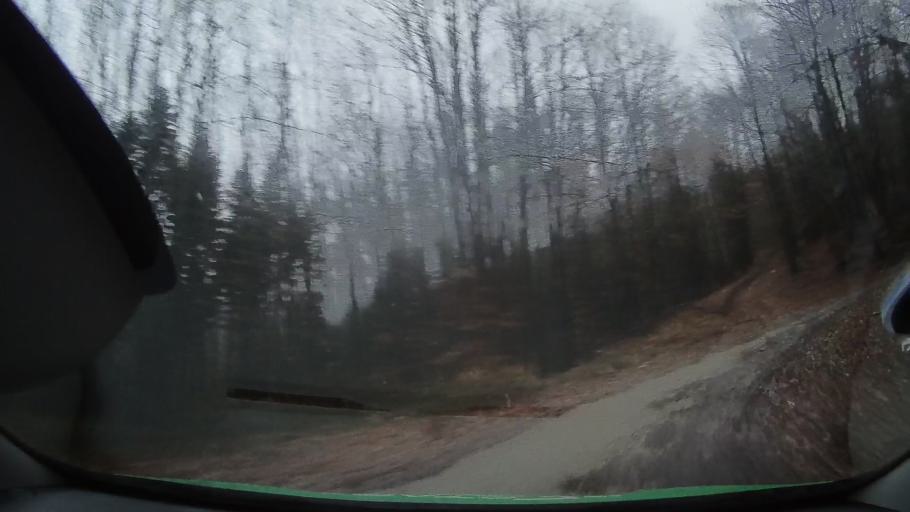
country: RO
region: Alba
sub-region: Comuna Avram Iancu
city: Avram Iancu
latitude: 46.3144
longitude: 22.7916
